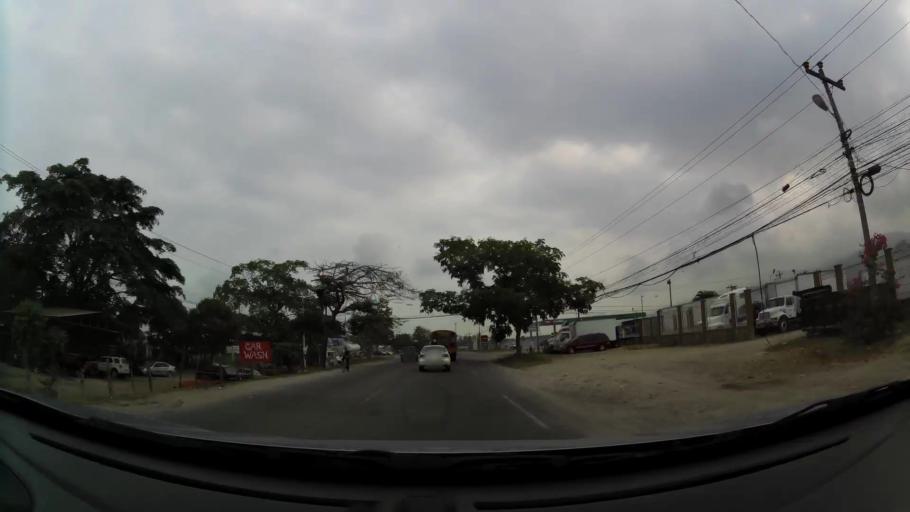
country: HN
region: Yoro
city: El Progreso
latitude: 15.4309
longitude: -87.7961
